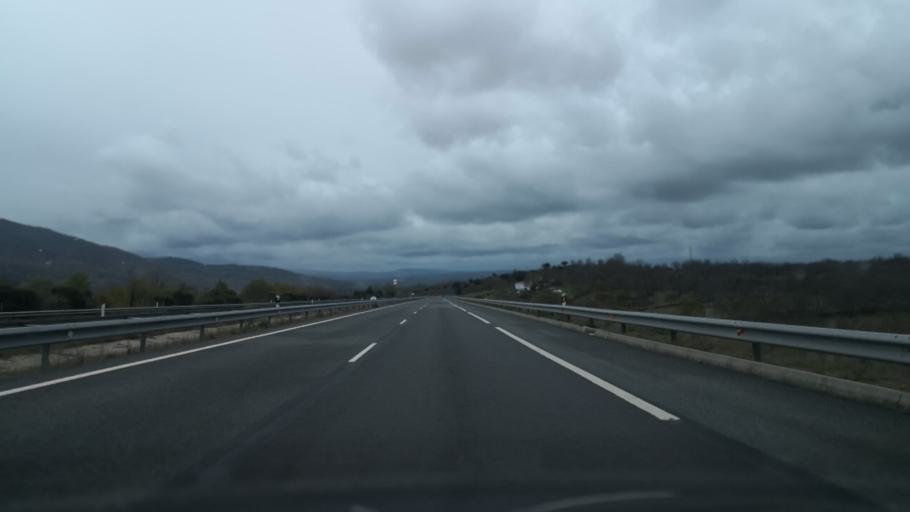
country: ES
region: Castille and Leon
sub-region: Provincia de Salamanca
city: Bejar
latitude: 40.3966
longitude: -5.7487
